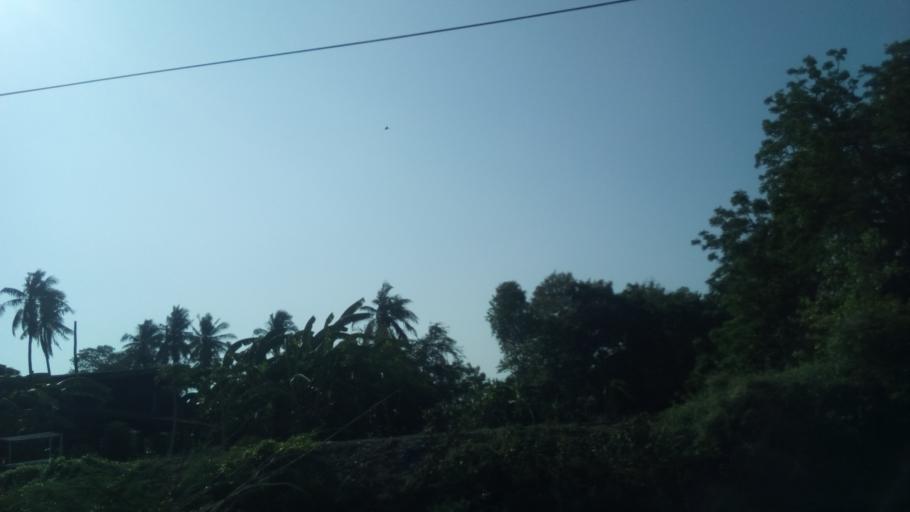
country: TH
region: Nonthaburi
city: Sai Noi
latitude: 13.9390
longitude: 100.3480
